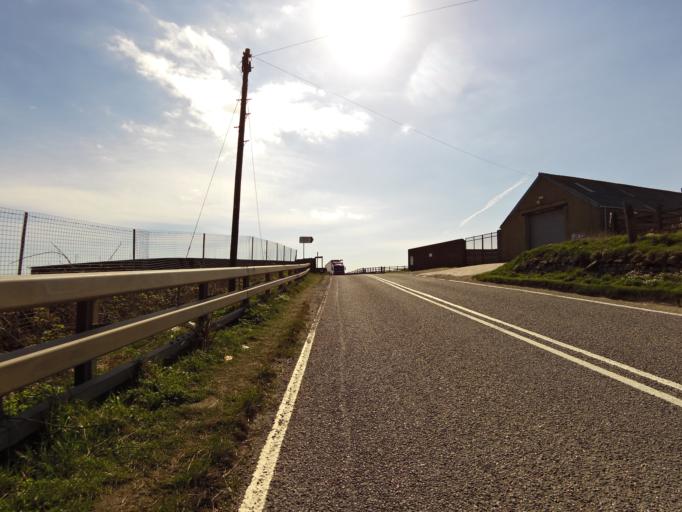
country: GB
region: Scotland
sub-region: Aberdeen City
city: Aberdeen
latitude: 57.1218
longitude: -2.0578
